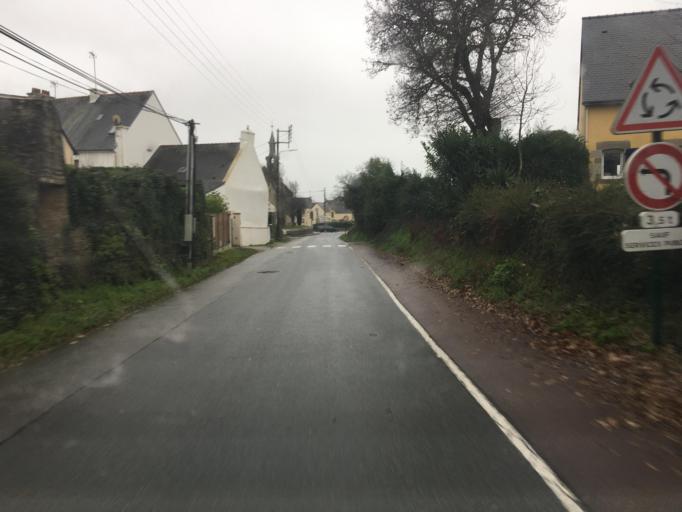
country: FR
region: Brittany
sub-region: Departement du Morbihan
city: Sarzeau
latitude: 47.5080
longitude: -2.6854
